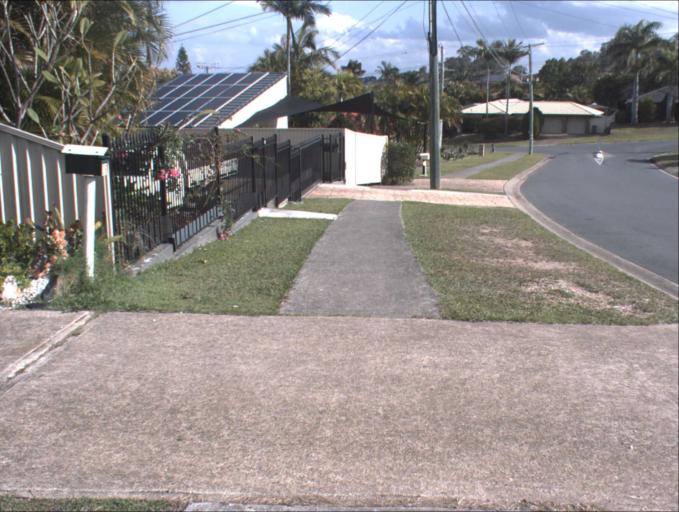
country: AU
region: Queensland
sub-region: Logan
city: Park Ridge South
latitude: -27.6722
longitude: 153.0355
